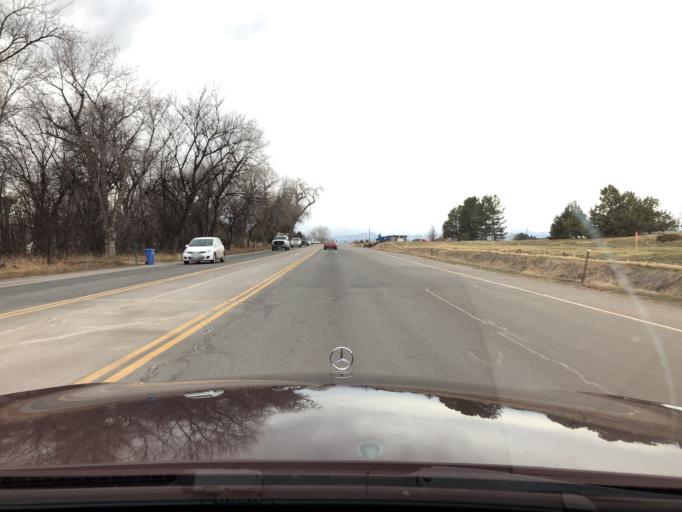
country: US
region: Colorado
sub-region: Boulder County
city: Louisville
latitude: 40.0147
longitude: -105.1239
